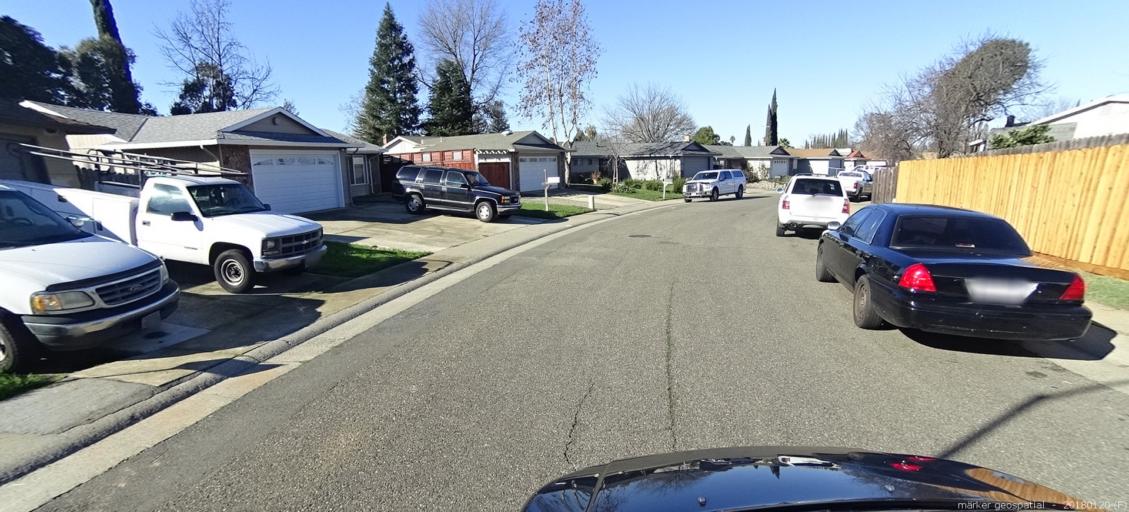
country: US
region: California
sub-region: Sacramento County
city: Rancho Cordova
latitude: 38.5718
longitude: -121.3106
